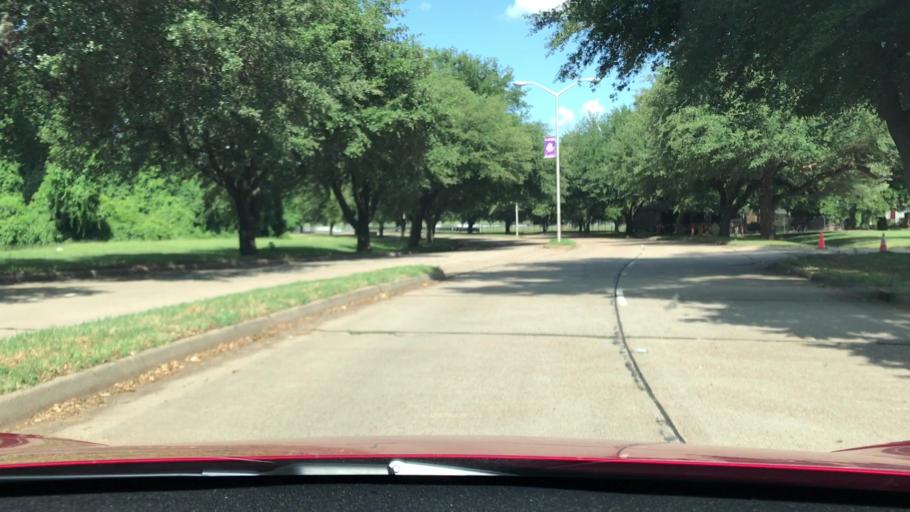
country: US
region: Louisiana
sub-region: Bossier Parish
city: Bossier City
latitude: 32.4317
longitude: -93.7047
